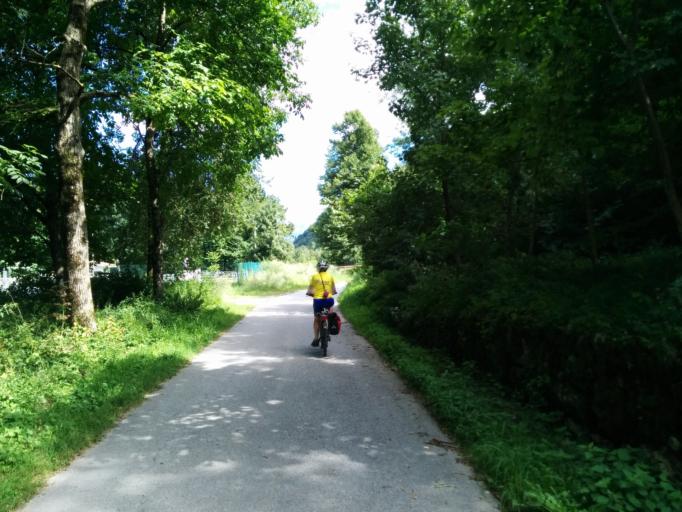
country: IT
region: Friuli Venezia Giulia
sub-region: Provincia di Udine
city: Lauco
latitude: 46.4064
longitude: 12.9449
